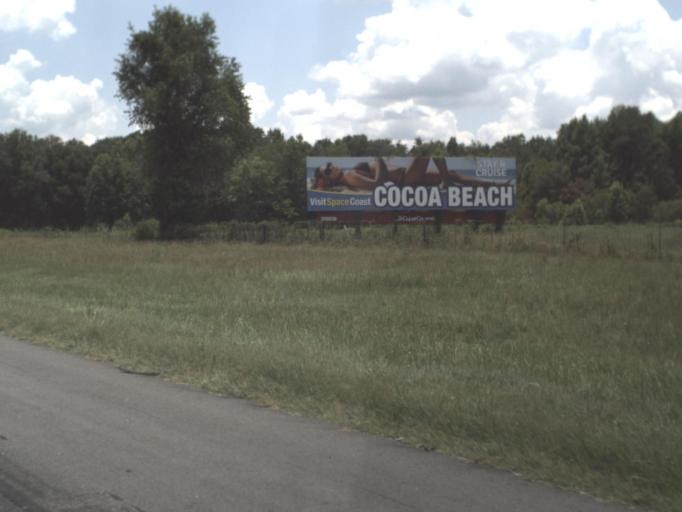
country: US
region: Florida
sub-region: Hamilton County
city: Jasper
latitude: 30.5286
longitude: -83.0681
